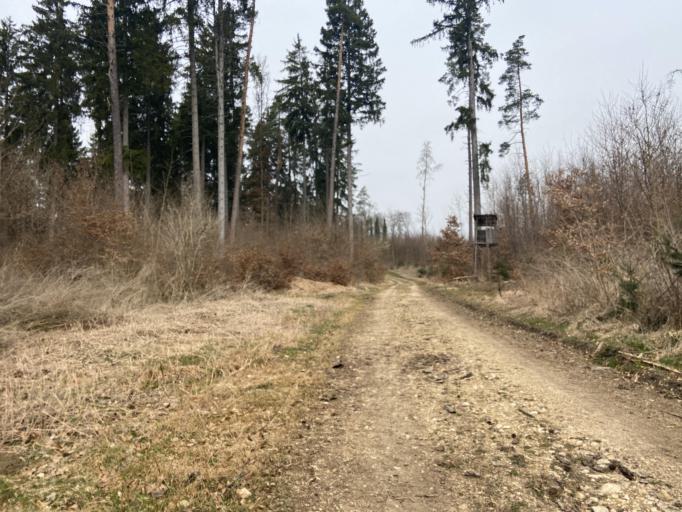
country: DE
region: Baden-Wuerttemberg
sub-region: Tuebingen Region
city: Bingen
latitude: 48.1058
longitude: 9.2483
